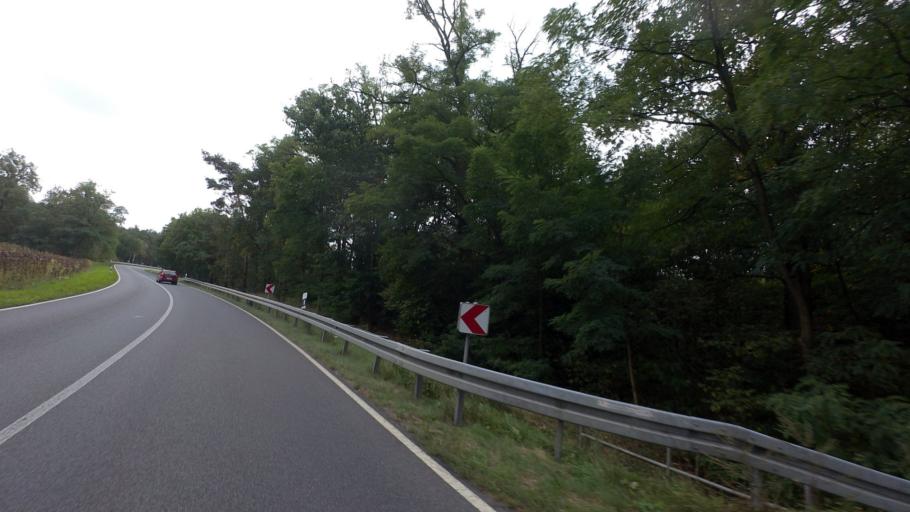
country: DE
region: Brandenburg
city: Sonnewalde
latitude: 51.7655
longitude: 13.6841
